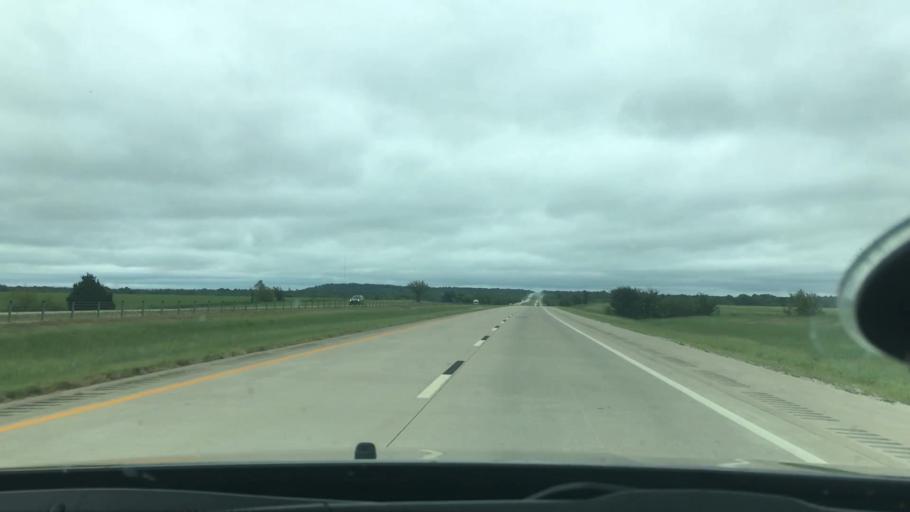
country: US
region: Oklahoma
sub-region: Muskogee County
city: Warner
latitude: 35.4822
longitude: -95.2707
